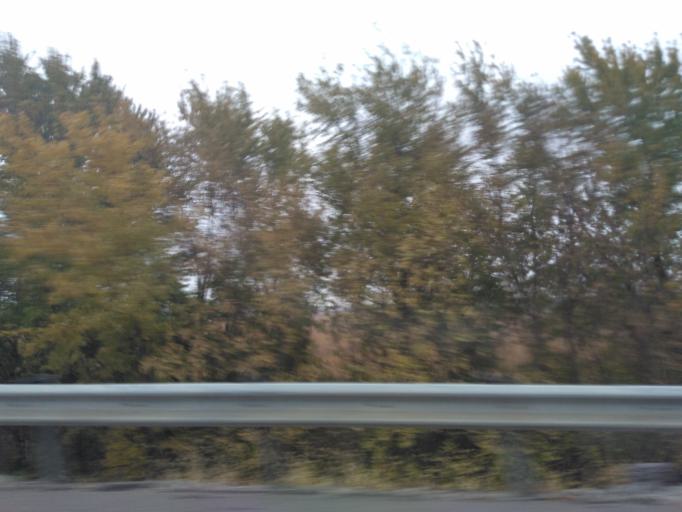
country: US
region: Missouri
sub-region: Saint Louis County
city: Oakville
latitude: 38.4840
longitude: -90.2660
